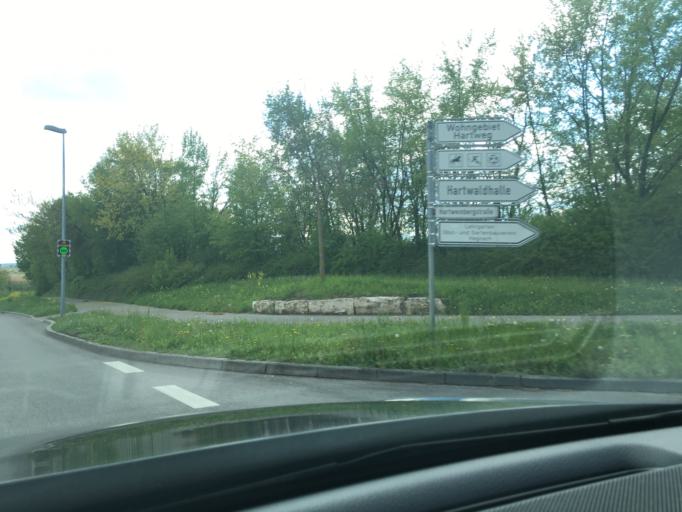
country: DE
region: Baden-Wuerttemberg
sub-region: Regierungsbezirk Stuttgart
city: Waiblingen
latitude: 48.8544
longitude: 9.2923
